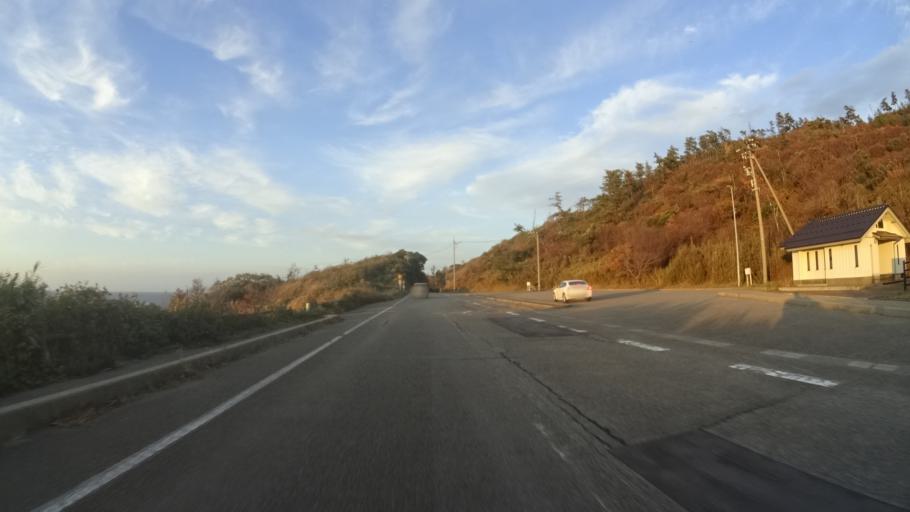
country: JP
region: Ishikawa
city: Nanao
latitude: 37.2174
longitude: 136.6962
